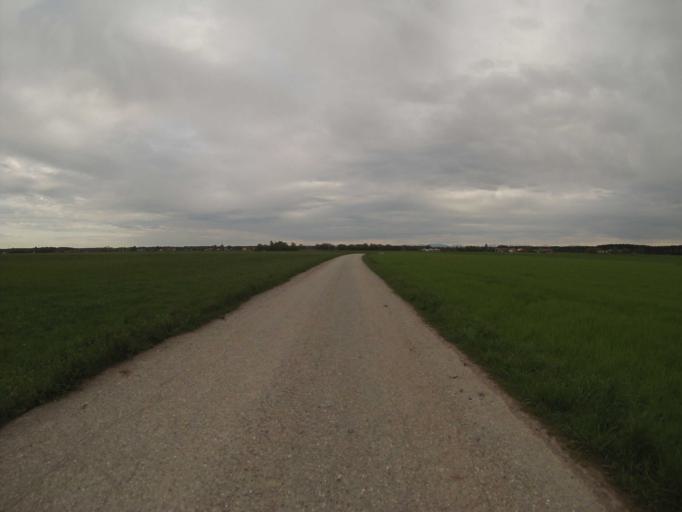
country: DE
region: Bavaria
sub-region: Upper Bavaria
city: Sauerlach
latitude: 47.9784
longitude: 11.6326
